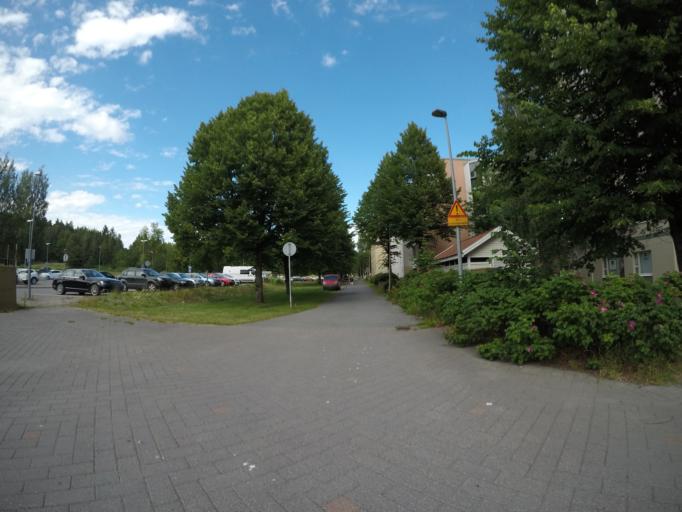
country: FI
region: Haeme
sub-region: Haemeenlinna
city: Haemeenlinna
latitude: 60.9853
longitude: 24.4173
